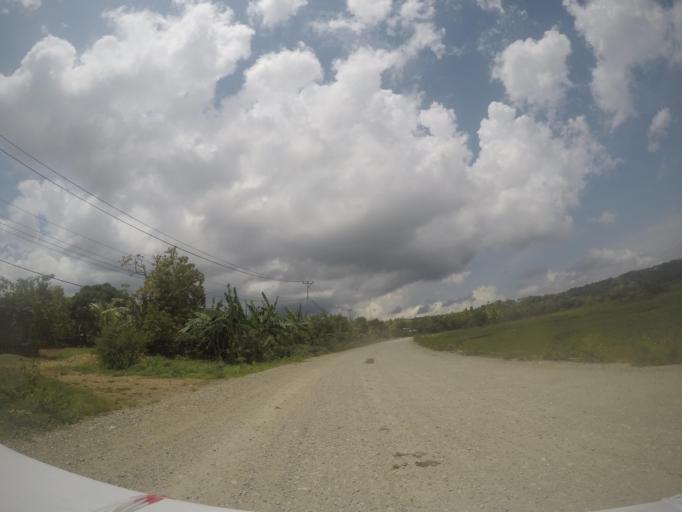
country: TL
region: Baucau
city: Venilale
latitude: -8.5703
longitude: 126.3944
